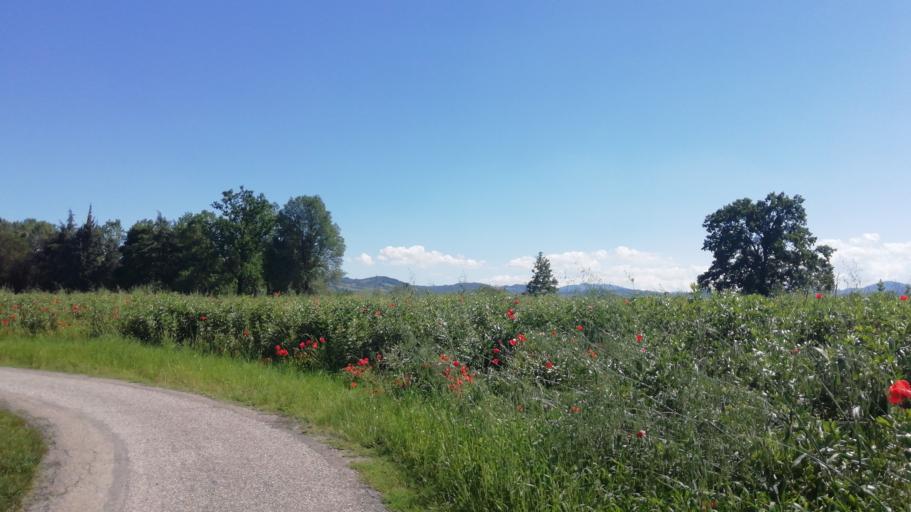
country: IT
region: Emilia-Romagna
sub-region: Provincia di Piacenza
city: Borgonovo Valtidone
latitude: 44.9946
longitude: 9.4559
